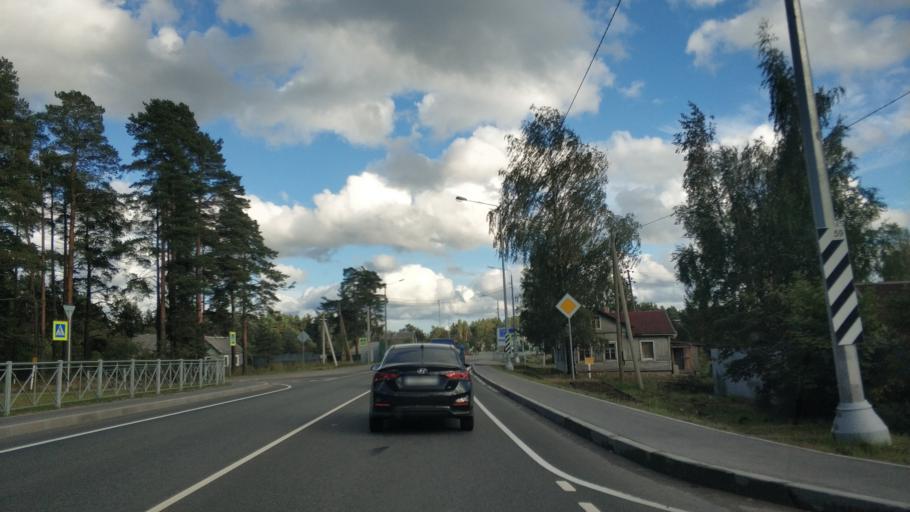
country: RU
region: Leningrad
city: Priozersk
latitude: 61.0074
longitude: 30.1752
